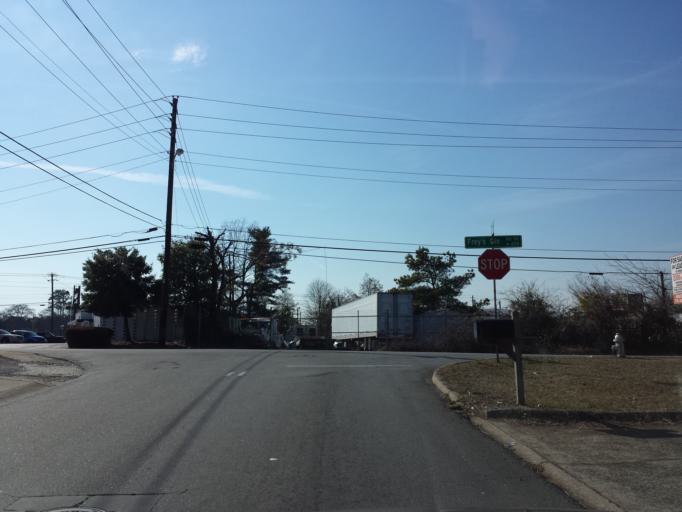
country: US
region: Georgia
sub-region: Cobb County
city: Marietta
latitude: 33.9455
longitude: -84.5162
